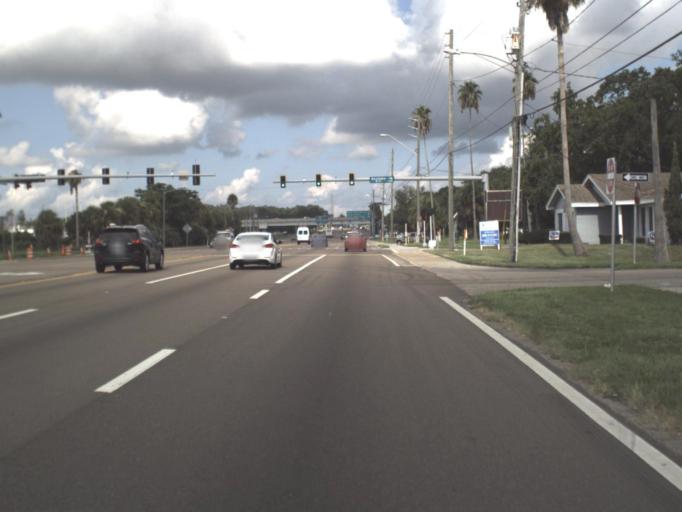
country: US
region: Florida
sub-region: Pinellas County
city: Safety Harbor
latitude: 27.9608
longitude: -82.7043
